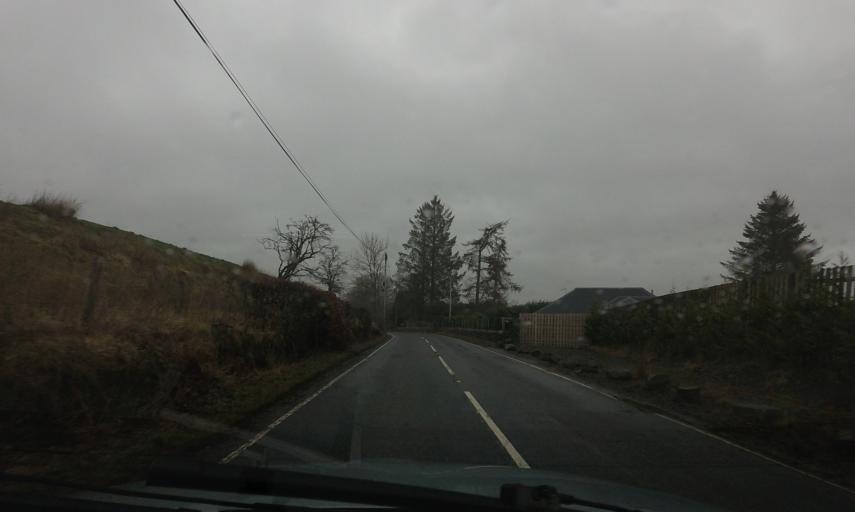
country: GB
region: Scotland
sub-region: Stirling
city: Balfron
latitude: 56.1024
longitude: -4.3589
